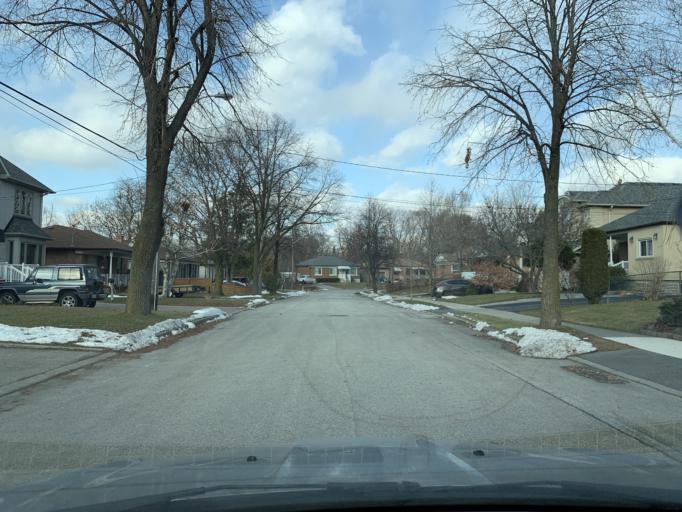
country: CA
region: Ontario
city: Toronto
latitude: 43.7001
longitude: -79.4858
